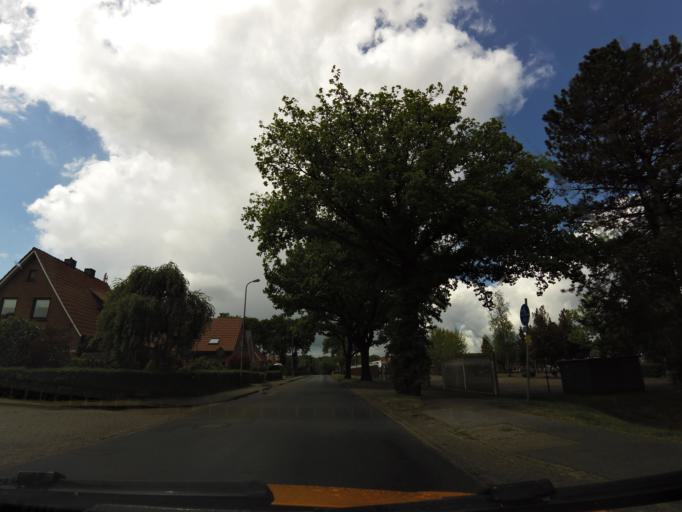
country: DE
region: Lower Saxony
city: Hude
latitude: 53.1024
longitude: 8.4744
